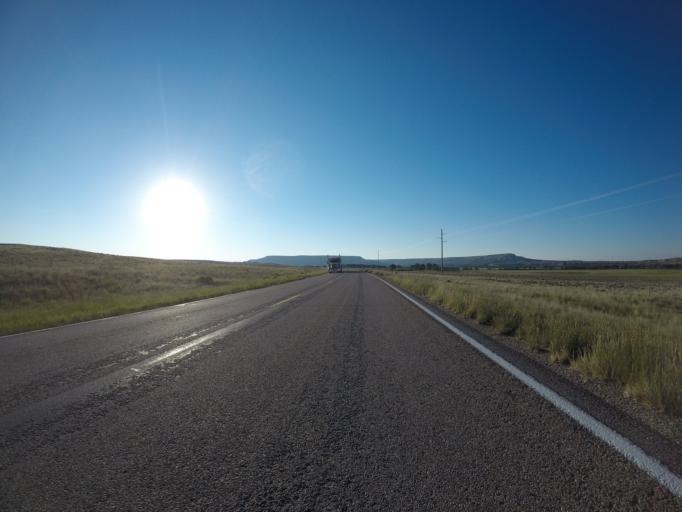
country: US
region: Wyoming
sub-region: Sublette County
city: Marbleton
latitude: 42.5721
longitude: -109.9737
